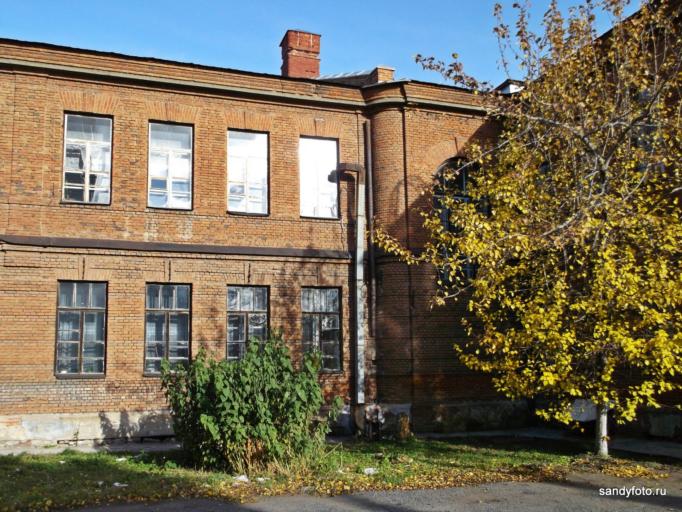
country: RU
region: Chelyabinsk
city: Troitsk
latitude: 54.0847
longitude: 61.5440
